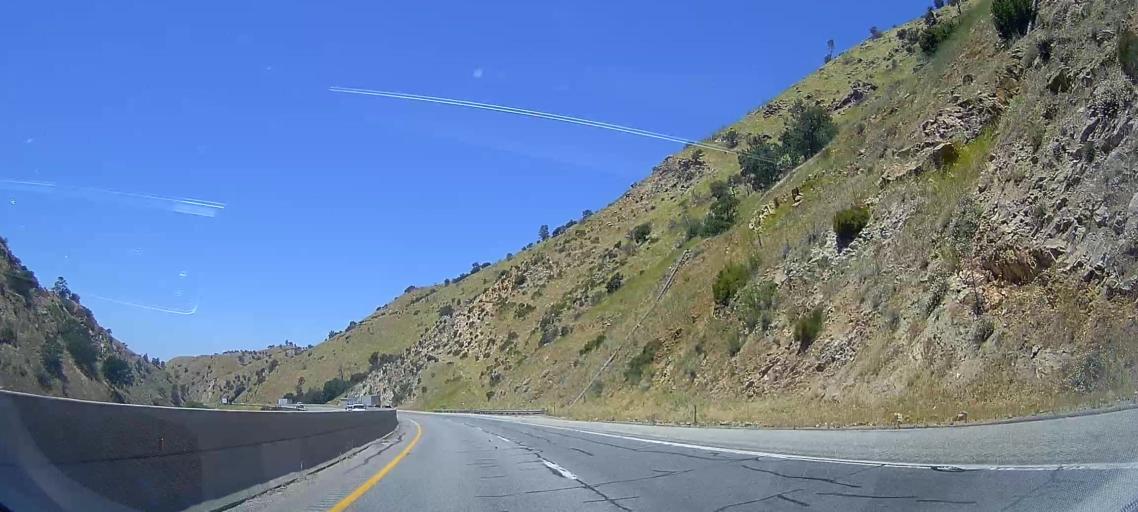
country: US
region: California
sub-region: Kern County
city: Golden Hills
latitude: 35.1767
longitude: -118.4811
